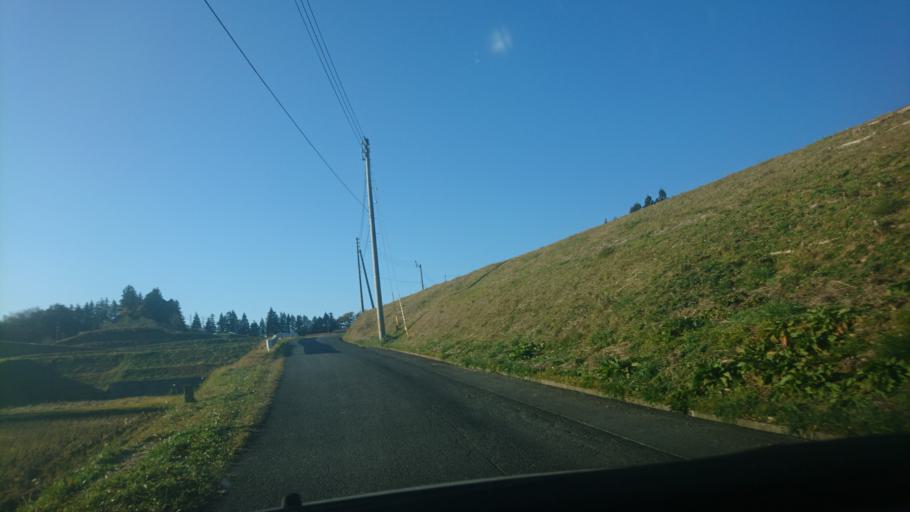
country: JP
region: Iwate
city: Ichinoseki
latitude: 38.8960
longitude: 141.1968
